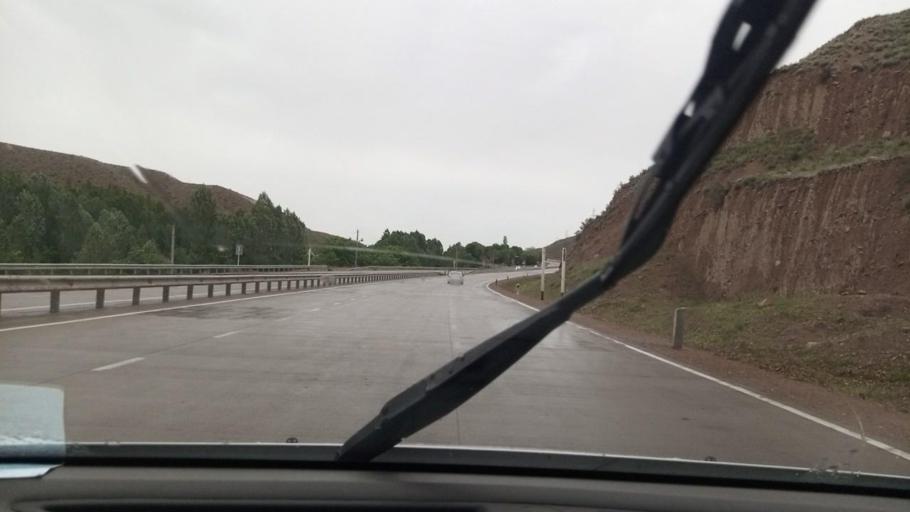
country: UZ
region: Namangan
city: Pop Shahri
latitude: 40.9500
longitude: 70.6788
